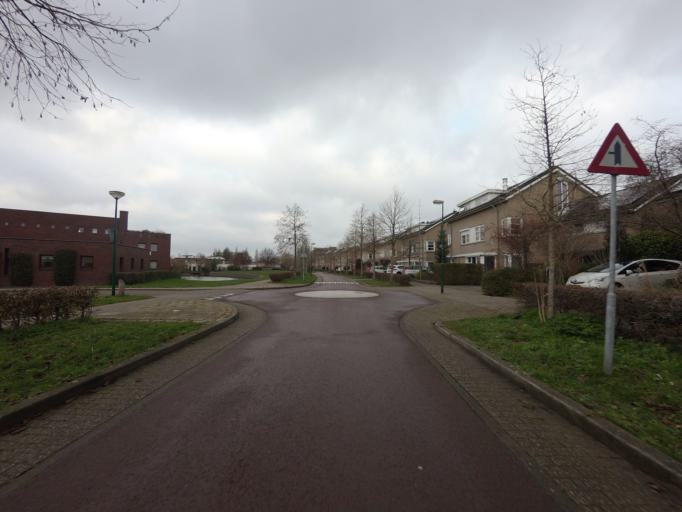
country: NL
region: Utrecht
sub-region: Gemeente Houten
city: Houten
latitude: 52.0237
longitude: 5.1920
